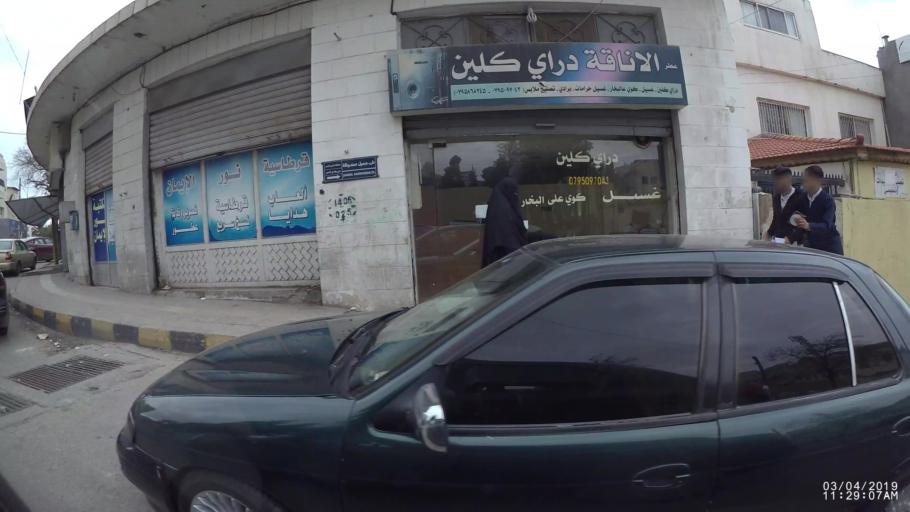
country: JO
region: Amman
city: Wadi as Sir
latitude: 31.9532
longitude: 35.8202
